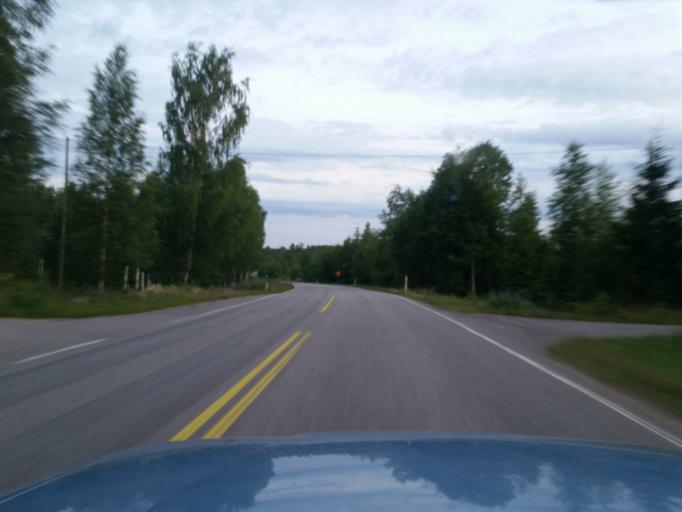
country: FI
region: Southern Savonia
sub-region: Savonlinna
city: Sulkava
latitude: 61.8270
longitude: 28.4407
